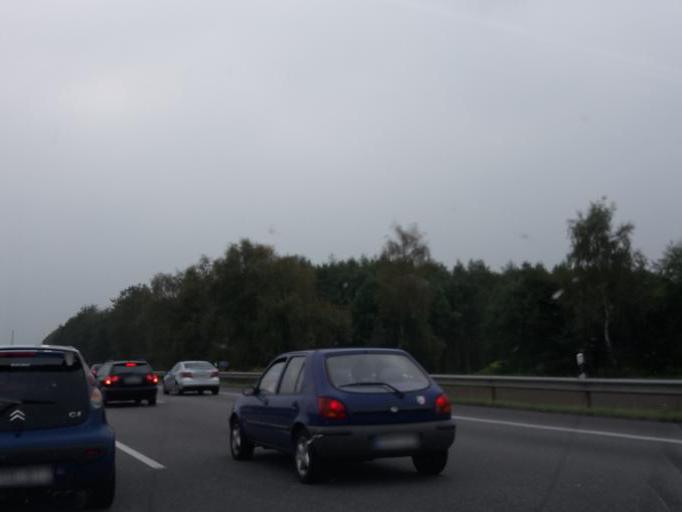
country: DE
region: Lower Saxony
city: Dinklage
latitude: 52.6790
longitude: 8.1715
